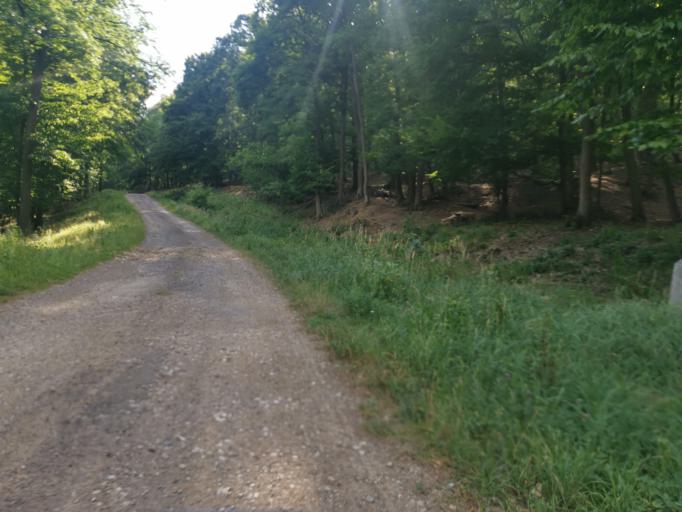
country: SK
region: Trnavsky
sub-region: Okres Senica
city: Senica
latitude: 48.7817
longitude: 17.3490
